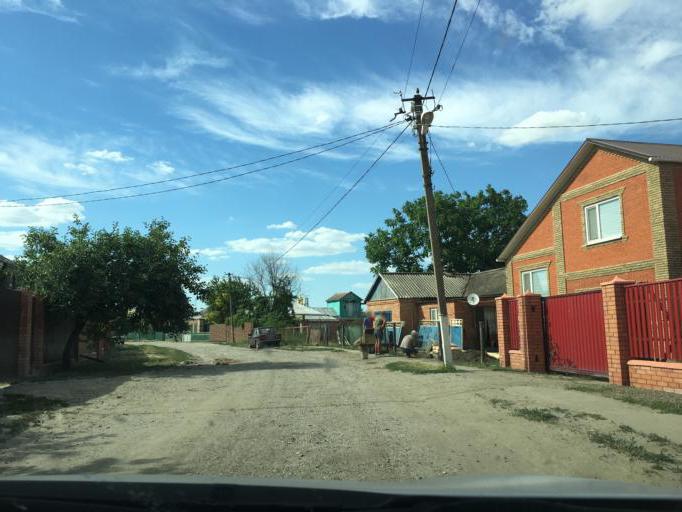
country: RU
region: Krasnodarskiy
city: Kushchevskaya
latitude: 46.5634
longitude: 39.6438
